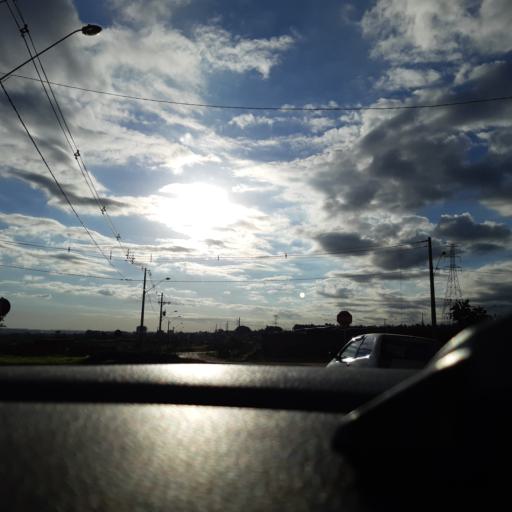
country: BR
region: Sao Paulo
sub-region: Ourinhos
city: Ourinhos
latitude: -23.0025
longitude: -49.8414
